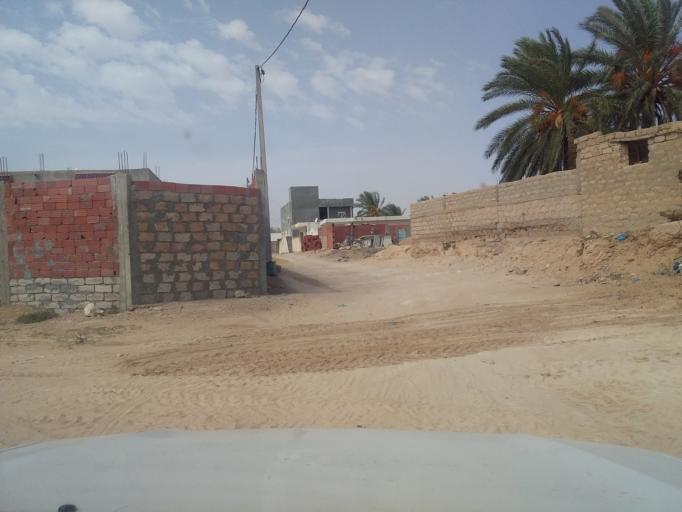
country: TN
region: Qabis
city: Matmata
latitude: 33.6147
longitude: 10.2770
